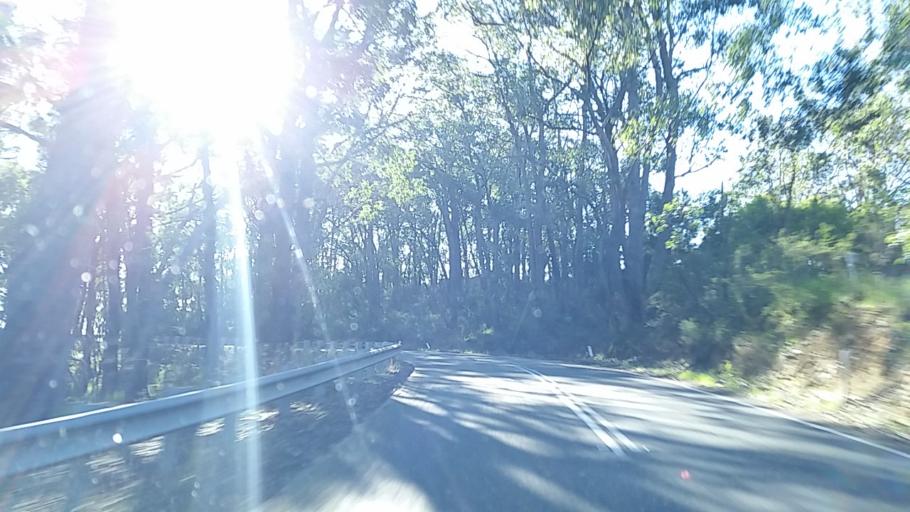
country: AU
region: South Australia
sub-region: Adelaide Hills
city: Adelaide Hills
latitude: -34.9340
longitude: 138.7327
